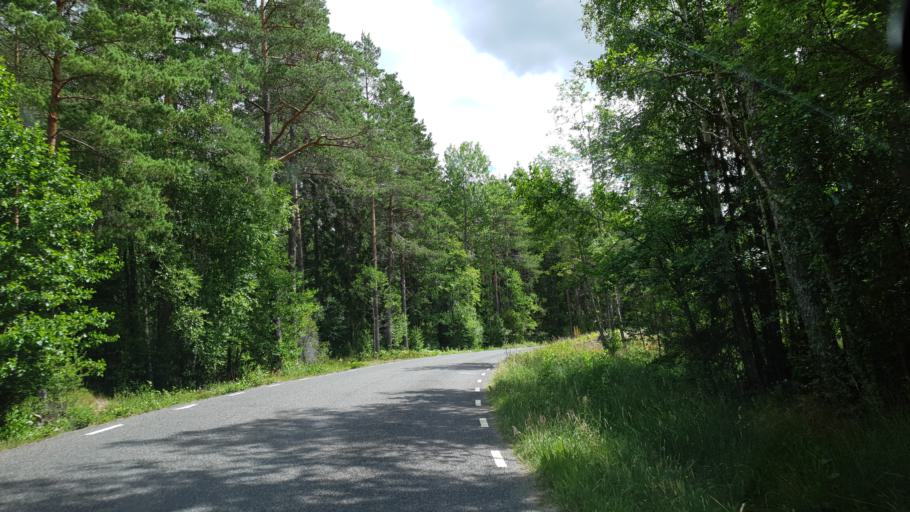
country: SE
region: Kronoberg
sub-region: Uppvidinge Kommun
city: Aseda
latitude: 57.1945
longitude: 15.4161
